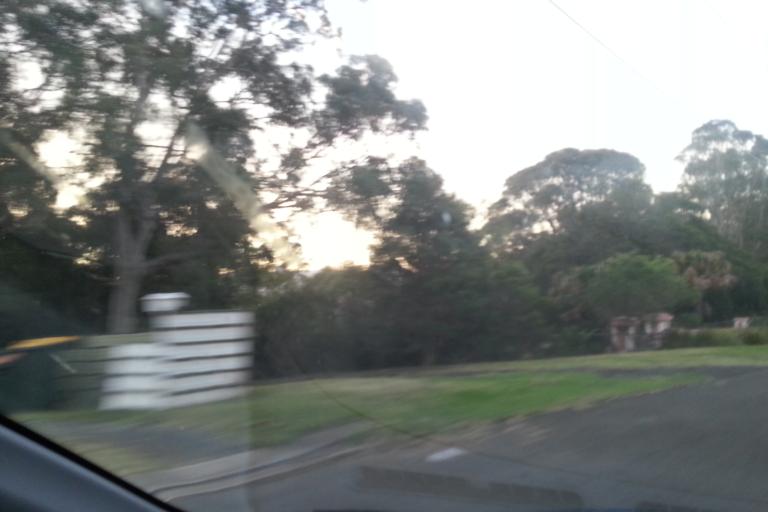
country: AU
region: New South Wales
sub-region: Wollongong
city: Cringila
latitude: -34.4778
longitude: 150.8838
